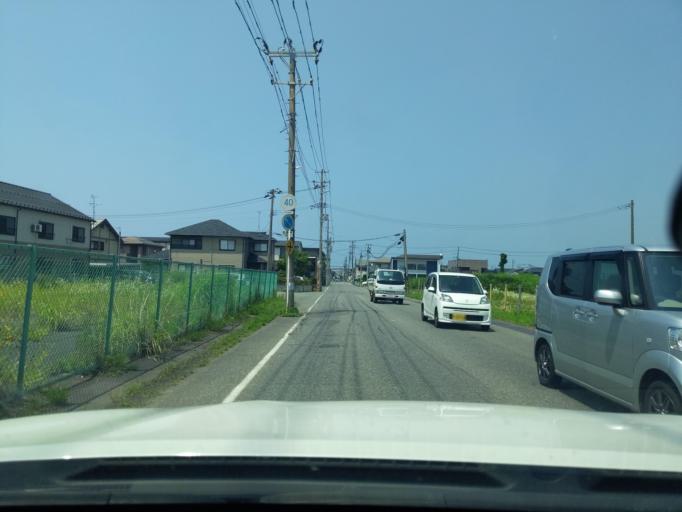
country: JP
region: Niigata
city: Kashiwazaki
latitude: 37.3636
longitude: 138.5816
